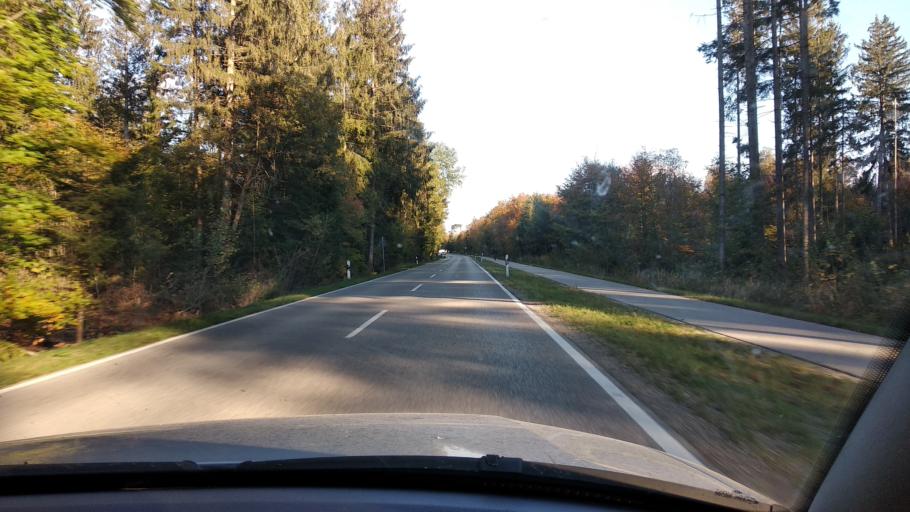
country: DE
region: Bavaria
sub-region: Upper Bavaria
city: Egmating
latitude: 48.0138
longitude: 11.7614
